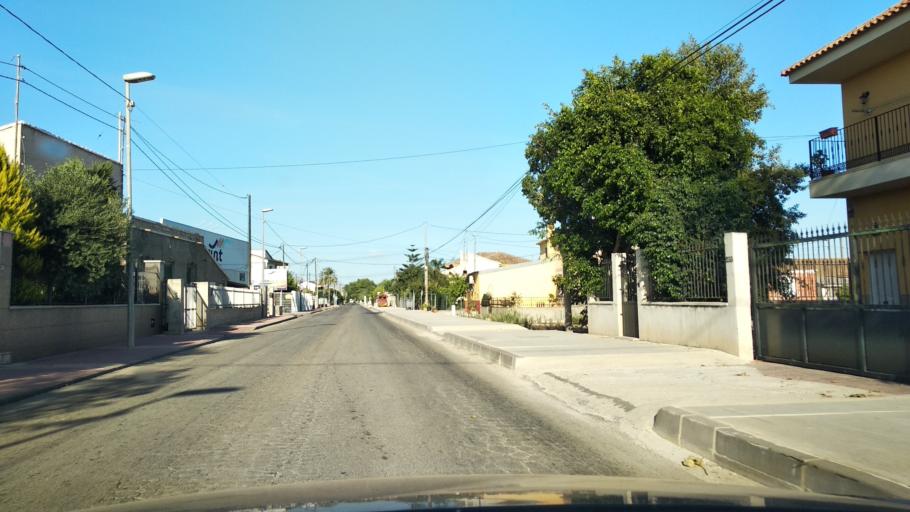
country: ES
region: Murcia
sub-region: Murcia
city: Santomera
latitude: 38.0425
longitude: -1.0427
